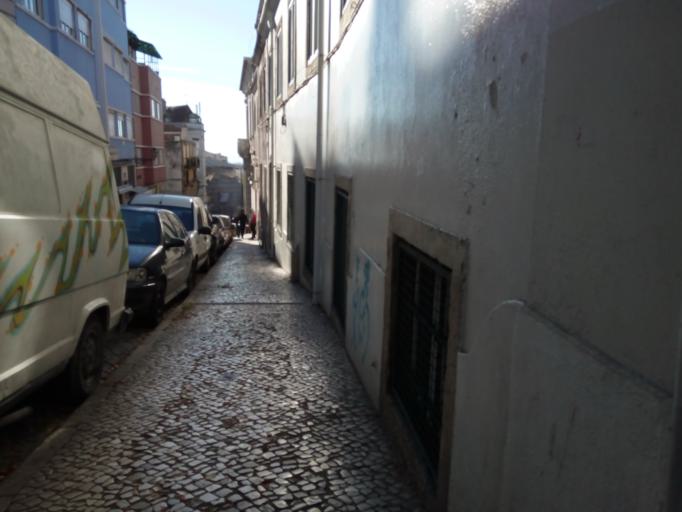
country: PT
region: Lisbon
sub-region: Lisbon
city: Lisbon
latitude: 38.7152
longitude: -9.1312
